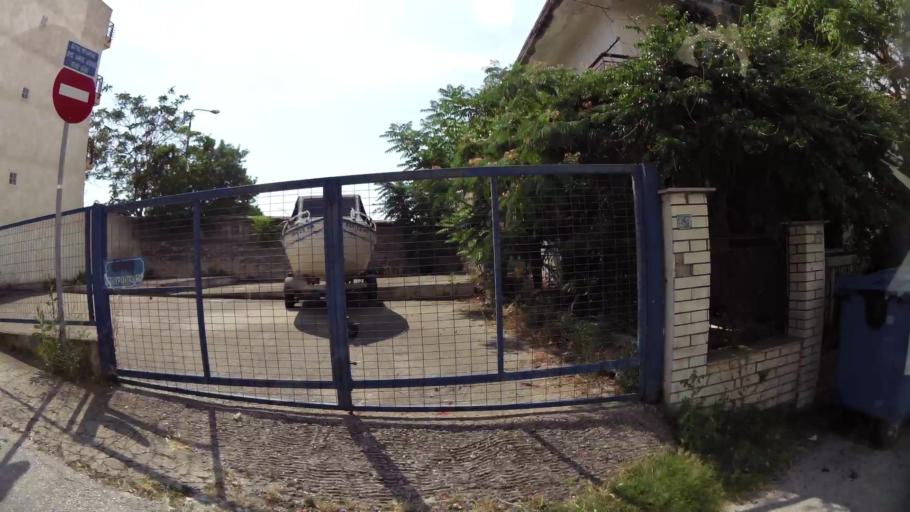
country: GR
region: Central Macedonia
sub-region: Nomos Thessalonikis
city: Polichni
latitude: 40.6664
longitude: 22.9433
